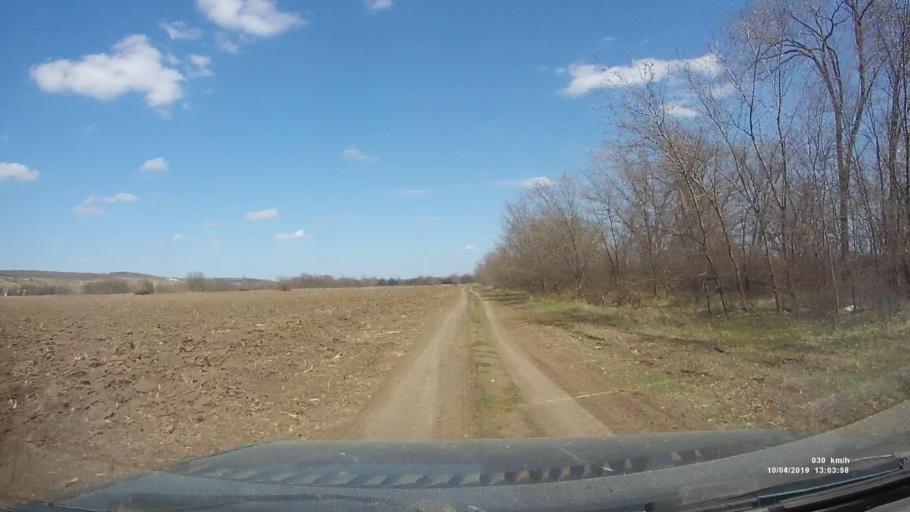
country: RU
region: Rostov
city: Masalovka
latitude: 48.3840
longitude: 40.2348
